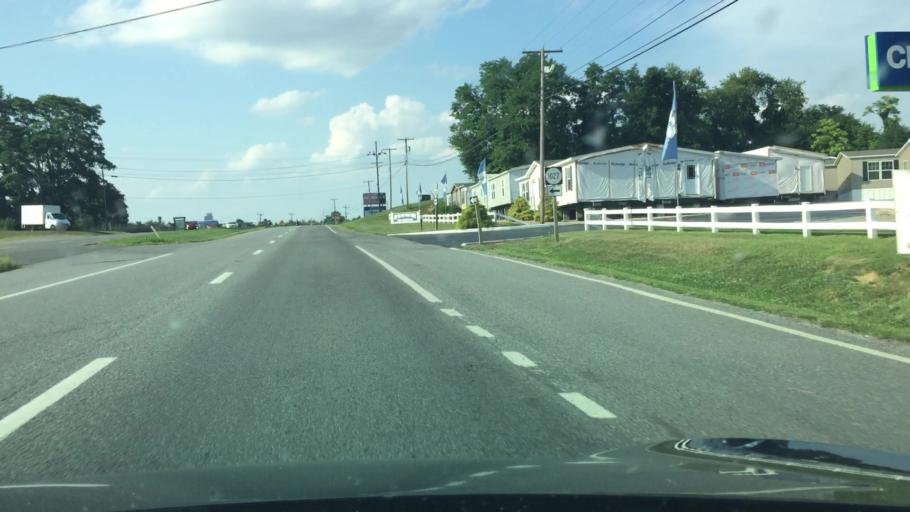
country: US
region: Virginia
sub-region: Pulaski County
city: Dublin
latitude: 37.0891
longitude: -80.6884
